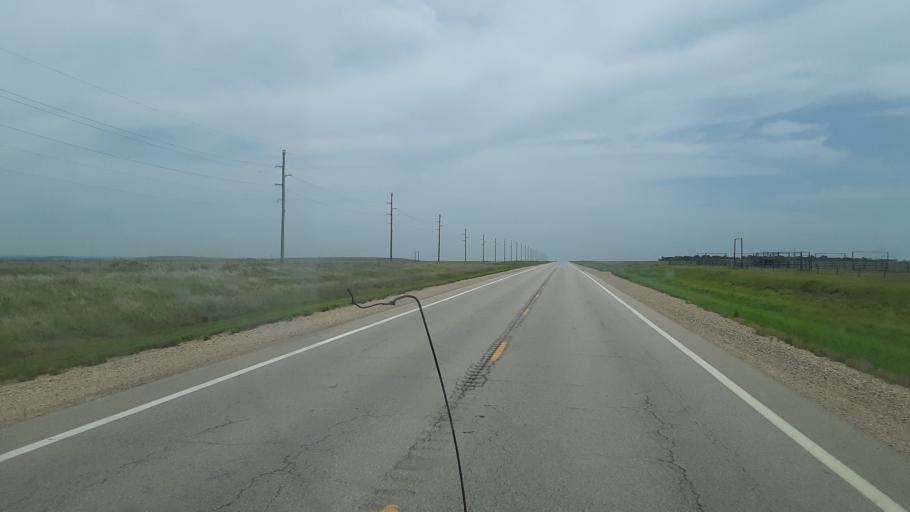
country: US
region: Kansas
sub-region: Greenwood County
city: Eureka
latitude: 37.8371
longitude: -96.0262
